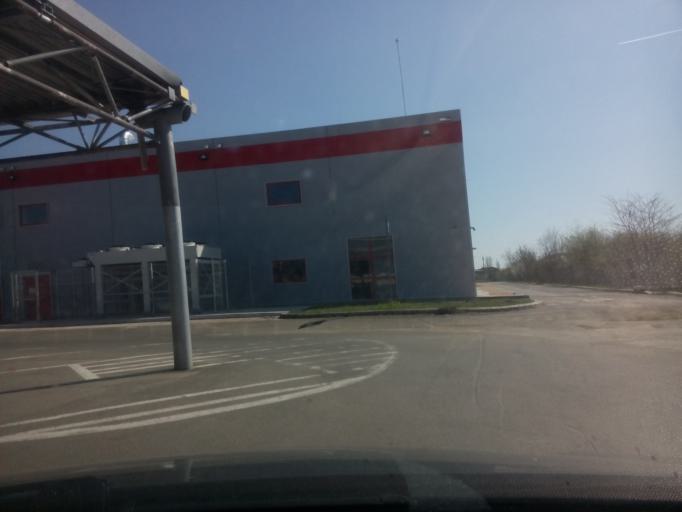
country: RO
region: Ilfov
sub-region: Comuna Pantelimon
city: Pantelimon
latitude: 44.4521
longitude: 26.2215
